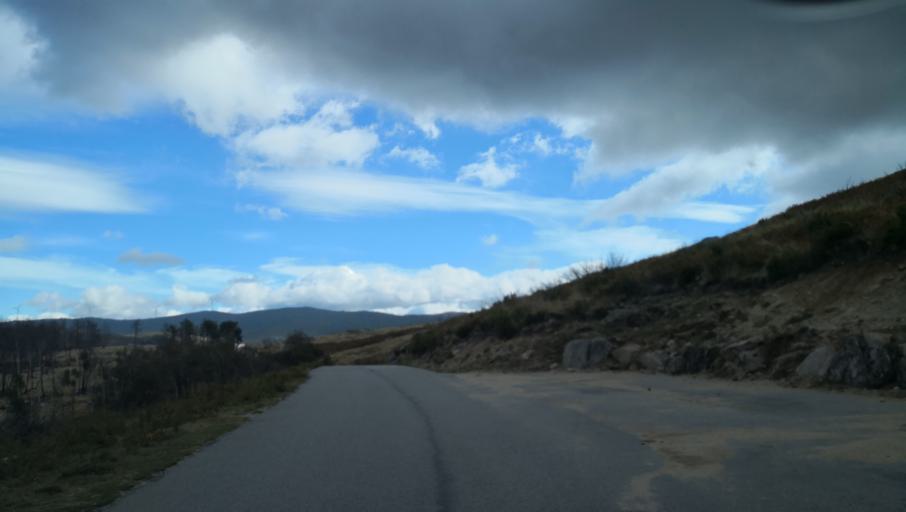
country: PT
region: Vila Real
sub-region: Vila Real
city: Vila Real
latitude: 41.3749
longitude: -7.8215
